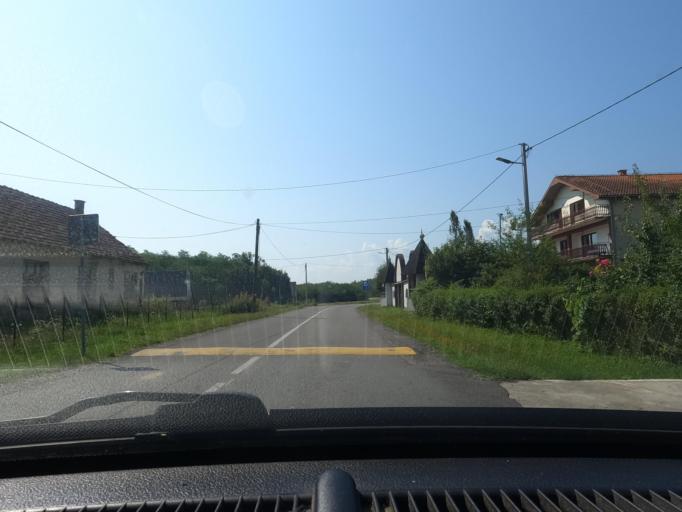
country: RS
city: Kozjak
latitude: 44.5554
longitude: 19.2958
